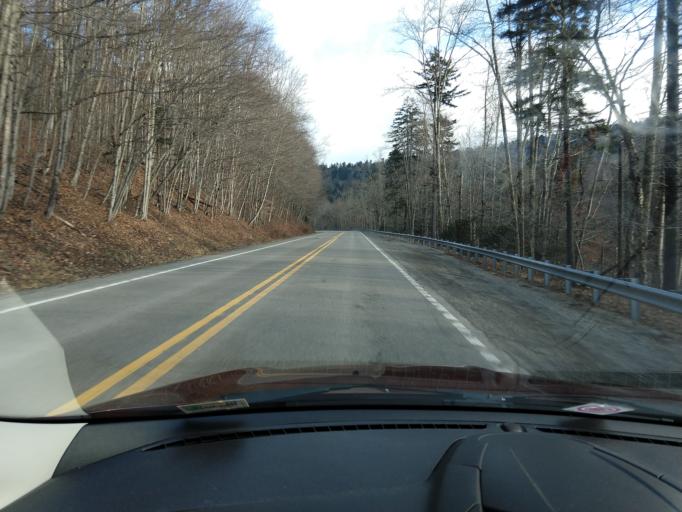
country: US
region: West Virginia
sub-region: Randolph County
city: Elkins
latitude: 38.6245
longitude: -79.8683
